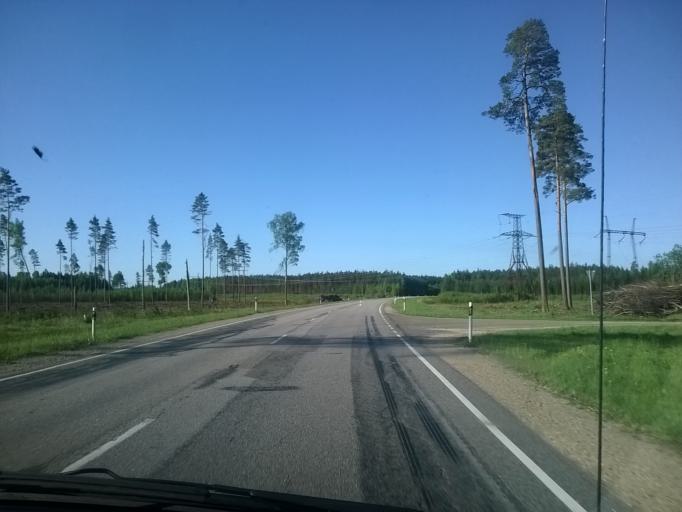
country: EE
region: Valgamaa
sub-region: Valga linn
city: Valga
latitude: 57.8815
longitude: 26.1632
